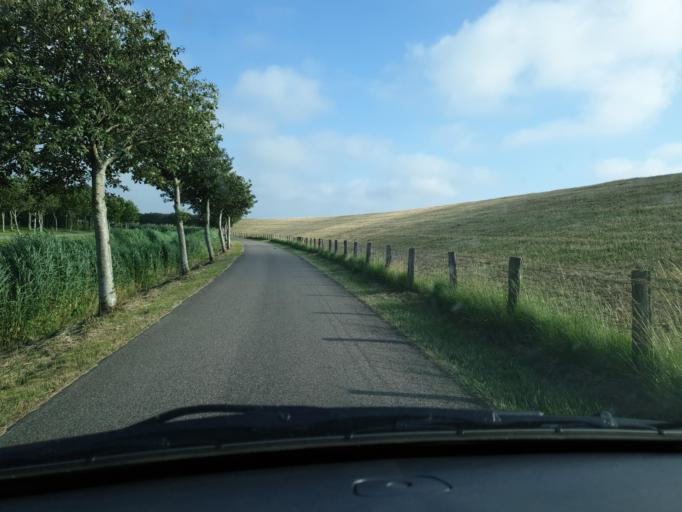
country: DE
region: Schleswig-Holstein
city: Friedrichskoog
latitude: 54.0271
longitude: 8.8383
